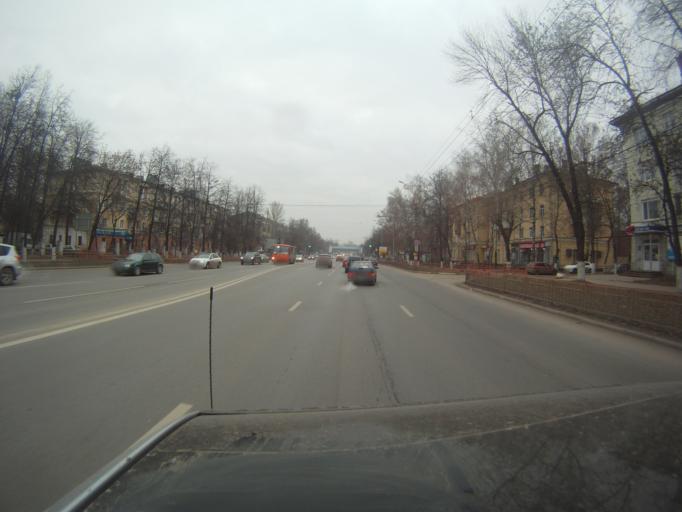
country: RU
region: Nizjnij Novgorod
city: Nizhniy Novgorod
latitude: 56.3030
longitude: 43.9844
